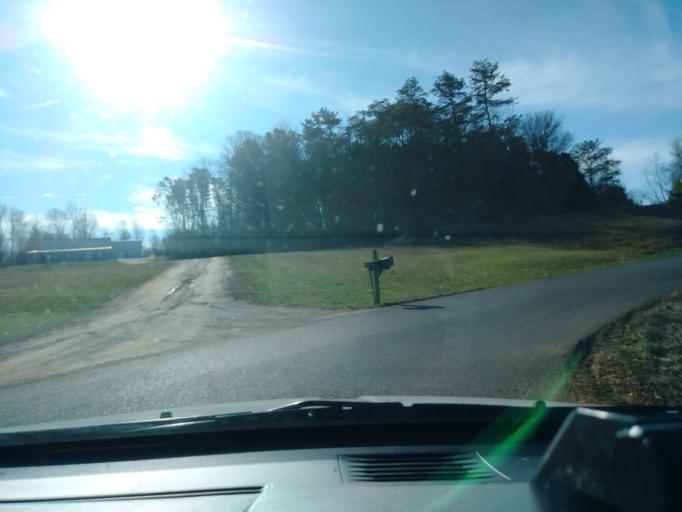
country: US
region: Tennessee
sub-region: Greene County
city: Greeneville
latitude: 36.0814
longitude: -82.8896
